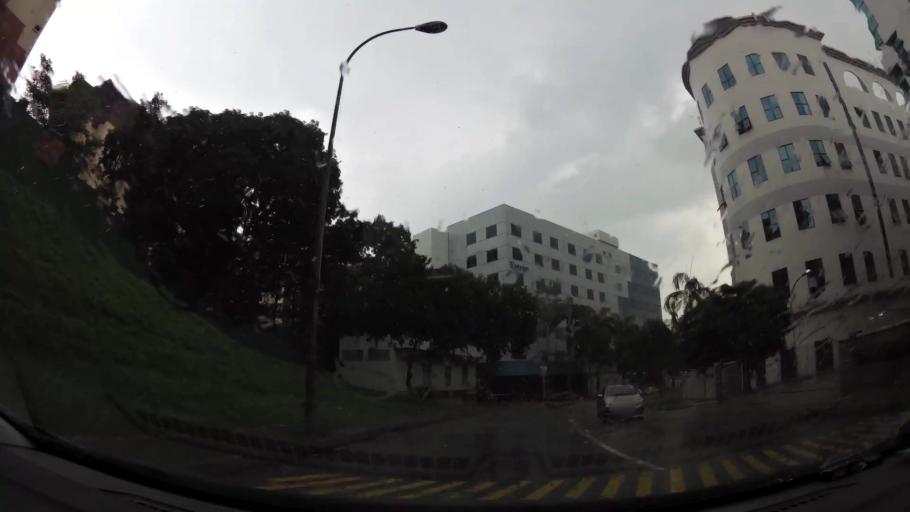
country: SG
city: Singapore
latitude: 1.3375
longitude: 103.8822
